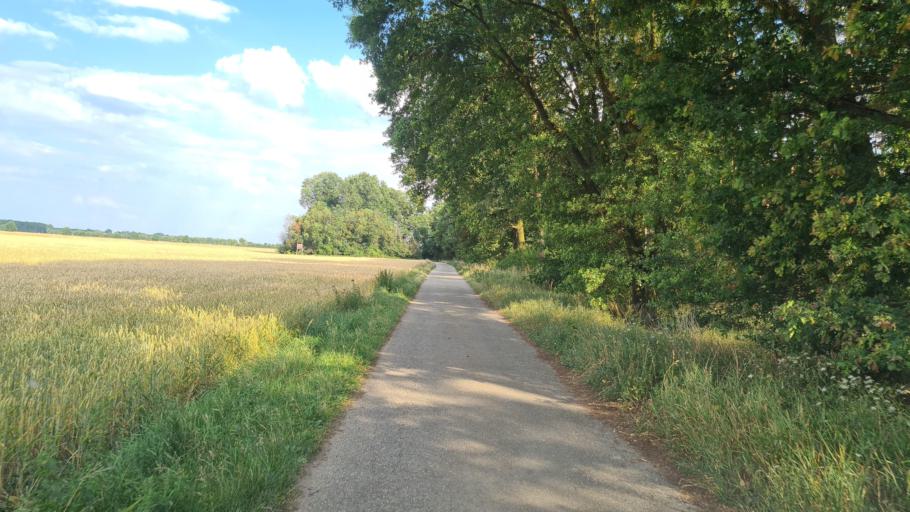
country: DE
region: Saxony-Anhalt
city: Pretzsch
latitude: 51.7607
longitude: 12.8504
